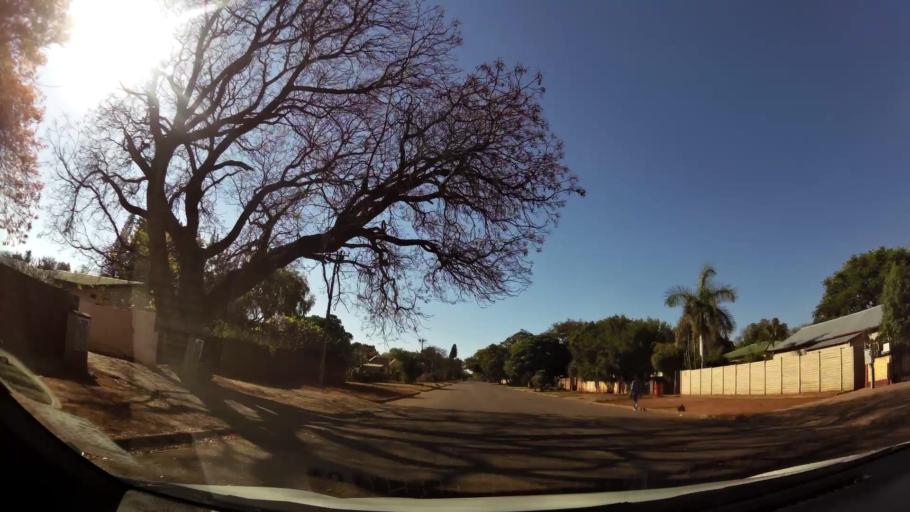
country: ZA
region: Limpopo
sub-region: Waterberg District Municipality
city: Mokopane
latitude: -24.1881
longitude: 29.0022
